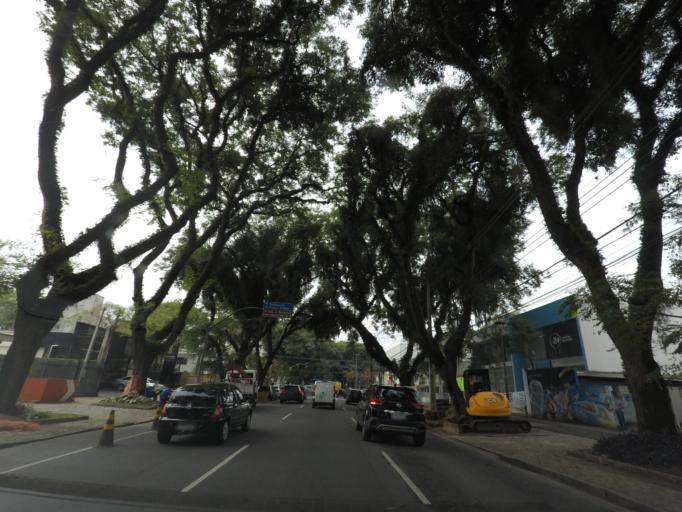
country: BR
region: Parana
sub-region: Curitiba
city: Curitiba
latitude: -25.4485
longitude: -49.2811
